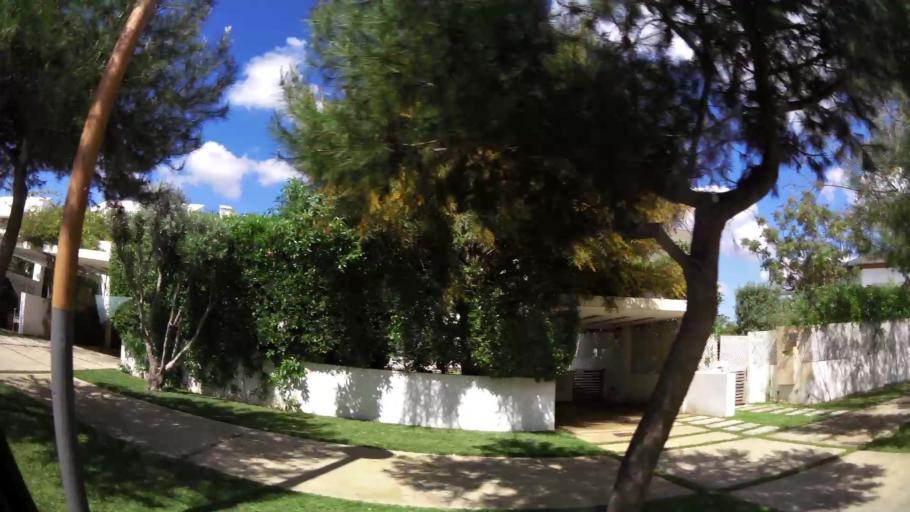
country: MA
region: Grand Casablanca
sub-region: Nouaceur
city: Bouskoura
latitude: 33.4945
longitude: -7.5976
